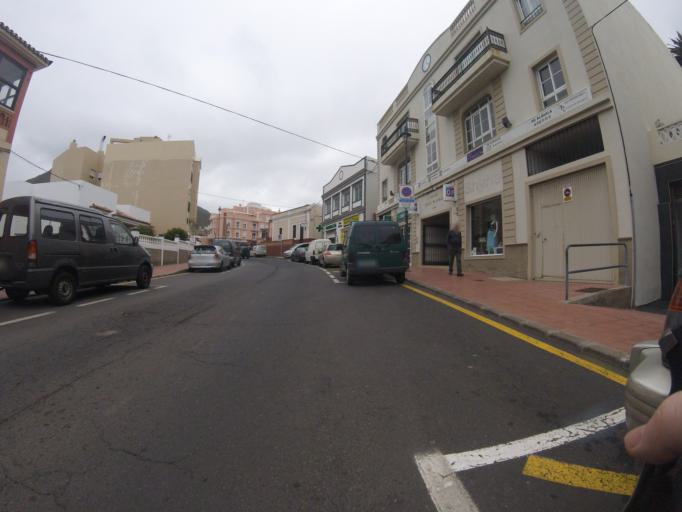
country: ES
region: Canary Islands
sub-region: Provincia de Santa Cruz de Tenerife
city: Tegueste
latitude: 28.5333
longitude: -16.3617
